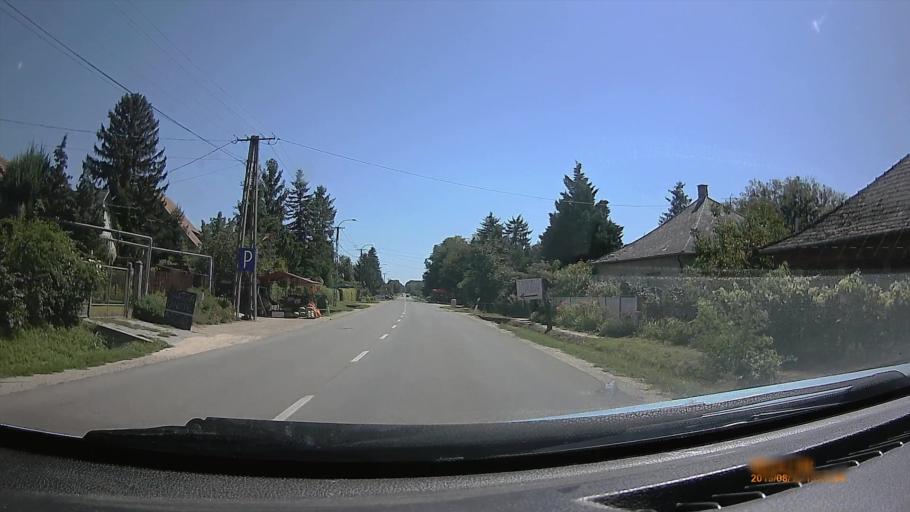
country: HU
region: Fejer
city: Cece
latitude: 46.7606
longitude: 18.6365
